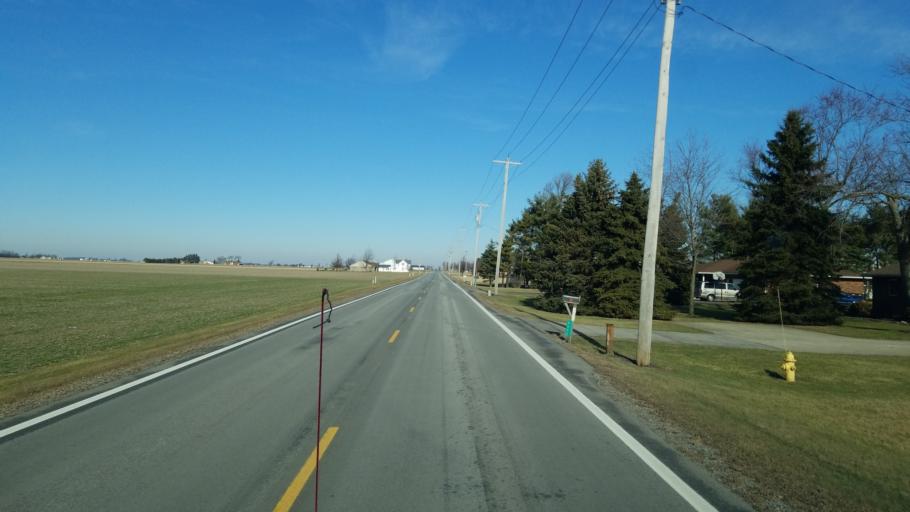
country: US
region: Ohio
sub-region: Putnam County
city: Leipsic
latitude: 41.1128
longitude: -83.9768
